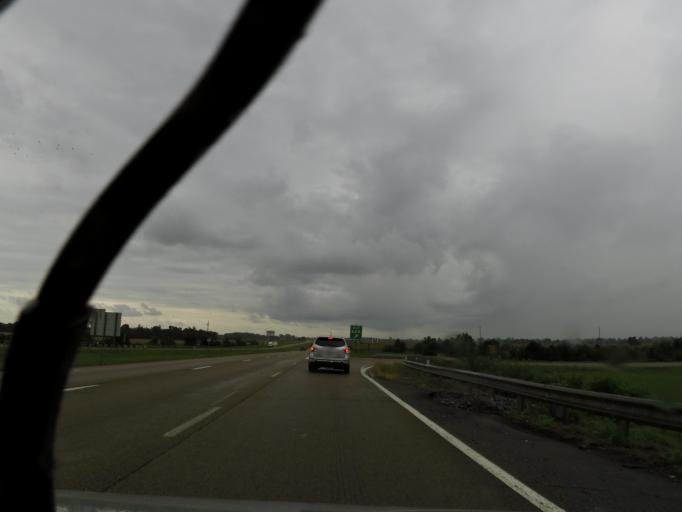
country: US
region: Missouri
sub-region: Scott County
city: Sikeston
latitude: 36.8727
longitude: -89.5334
